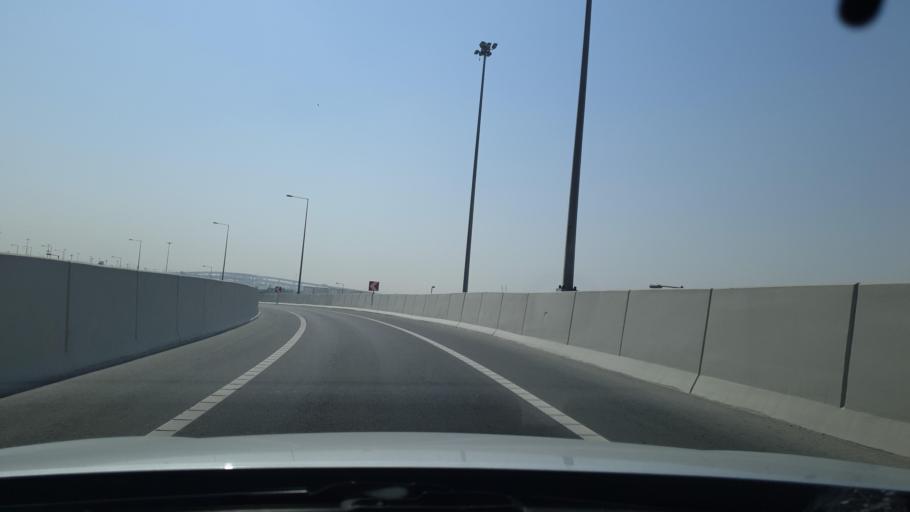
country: QA
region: Baladiyat ad Dawhah
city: Doha
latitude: 25.2208
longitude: 51.5322
